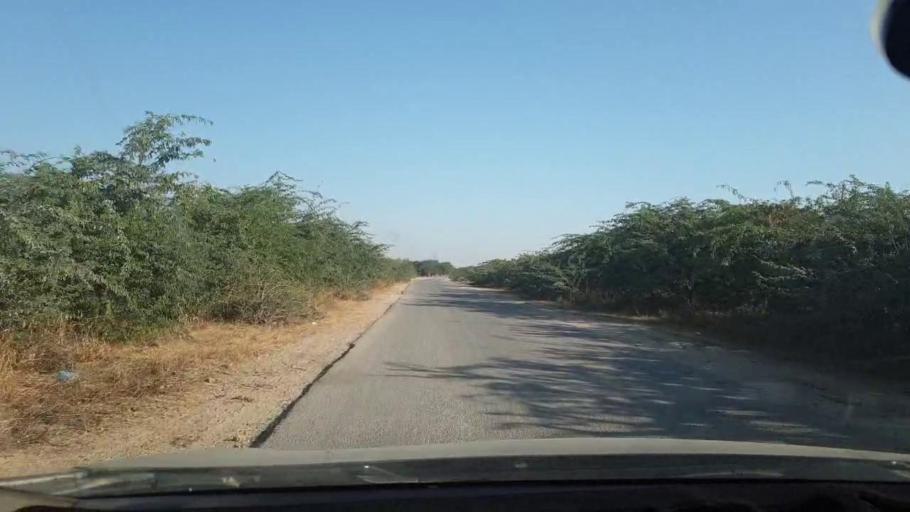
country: PK
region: Sindh
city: Malir Cantonment
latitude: 25.1658
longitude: 67.1965
